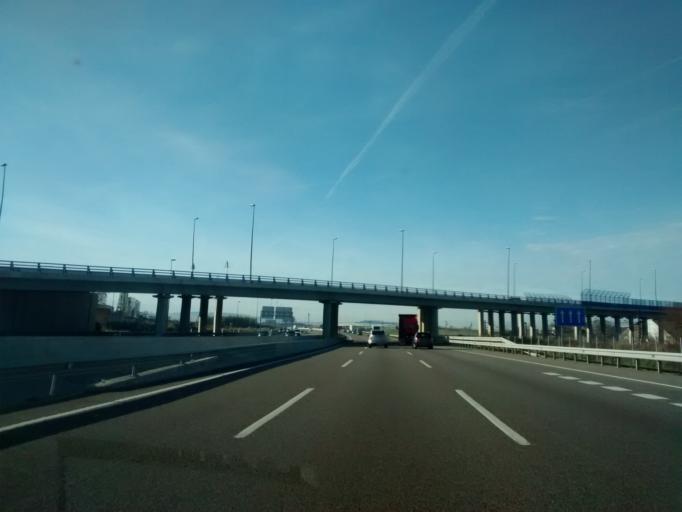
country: ES
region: Aragon
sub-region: Provincia de Zaragoza
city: Oliver-Valdefierro, Oliver, Valdefierro
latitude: 41.6599
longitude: -0.9489
